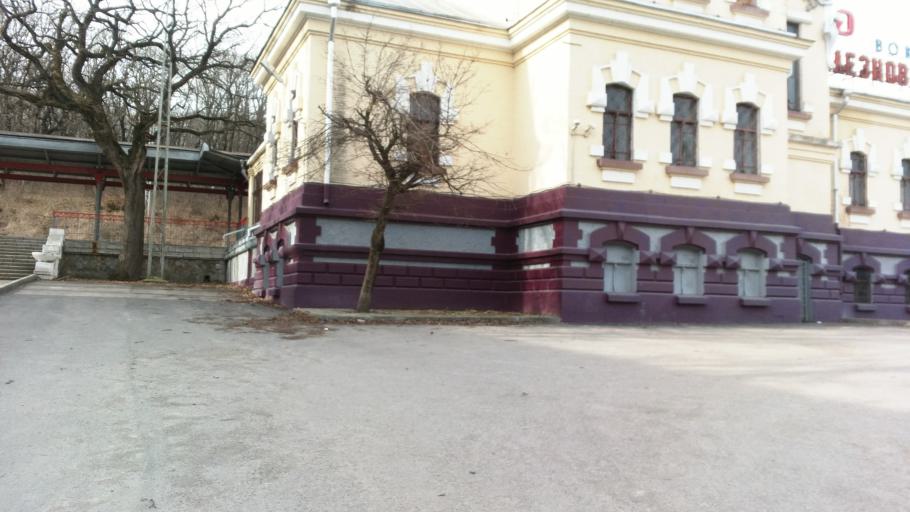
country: RU
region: Stavropol'skiy
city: Zheleznovodsk
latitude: 44.1312
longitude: 43.0269
